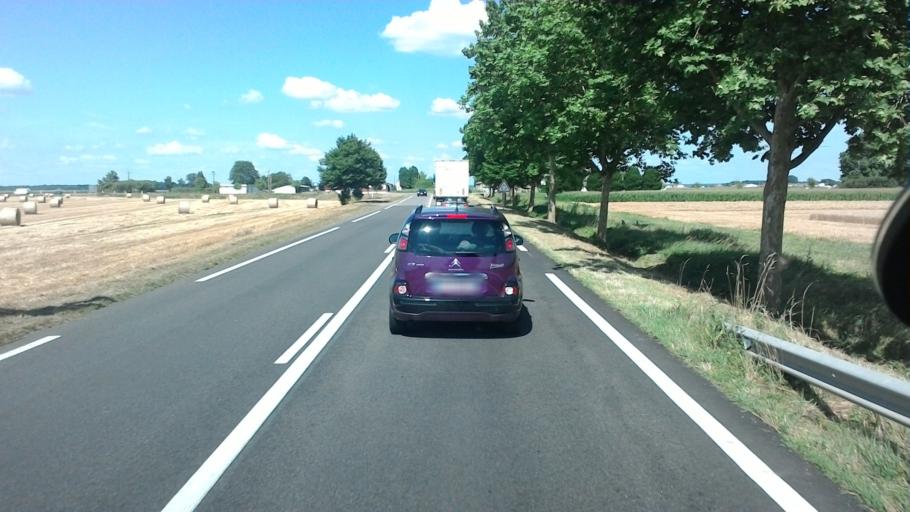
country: FR
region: Franche-Comte
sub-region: Departement du Jura
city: Saint-Aubin
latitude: 47.0020
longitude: 5.3528
